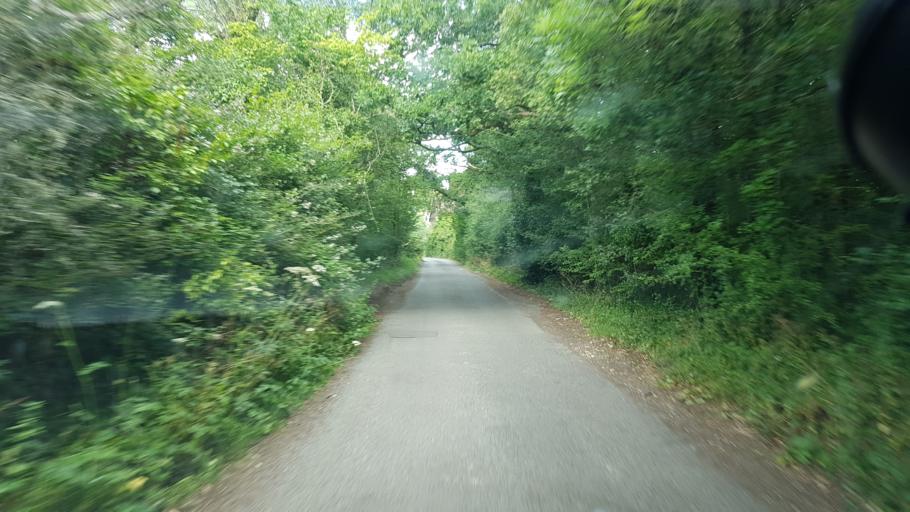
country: GB
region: England
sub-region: West Sussex
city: Billingshurst
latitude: 51.0271
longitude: -0.4320
